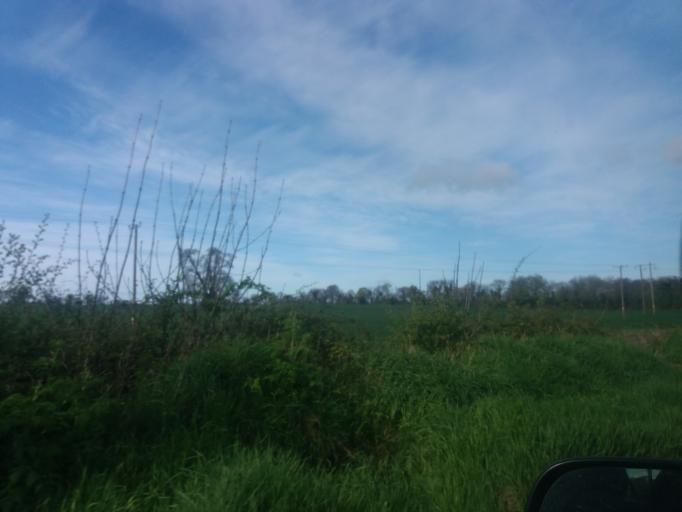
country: IE
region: Leinster
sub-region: An Mhi
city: Kells
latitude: 53.7237
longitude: -6.8600
